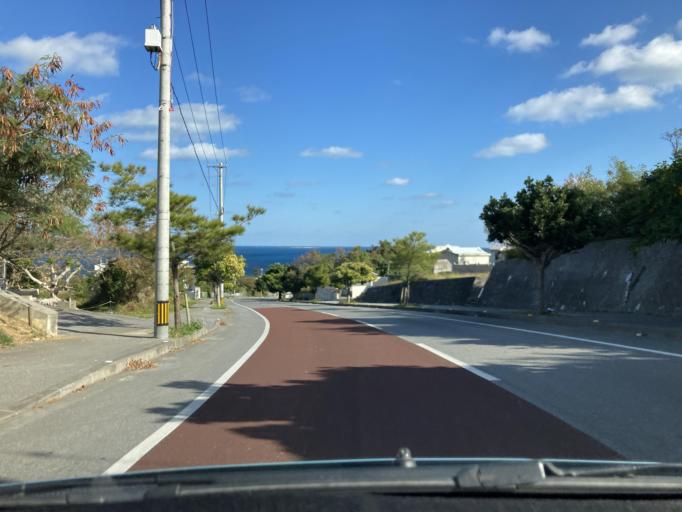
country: JP
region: Okinawa
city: Katsuren-haebaru
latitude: 26.3049
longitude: 127.9161
